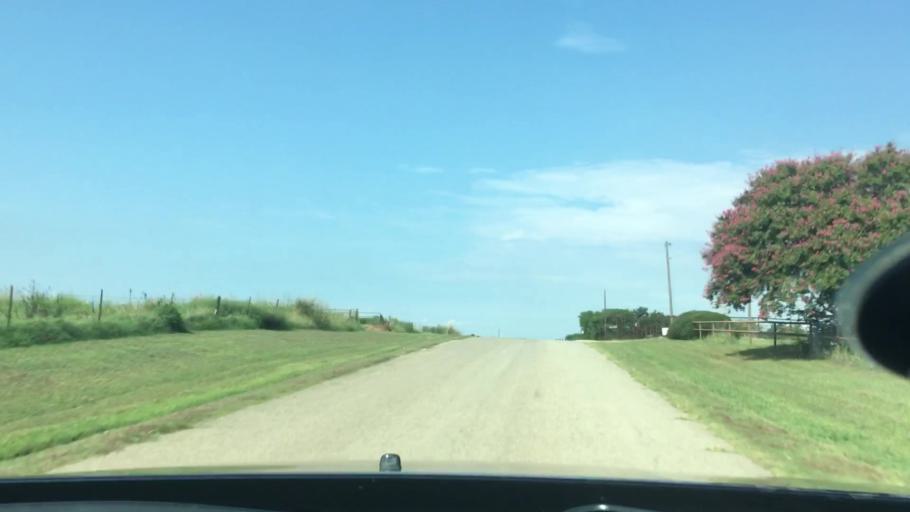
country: US
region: Oklahoma
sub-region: Bryan County
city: Calera
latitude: 33.9110
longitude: -96.4633
